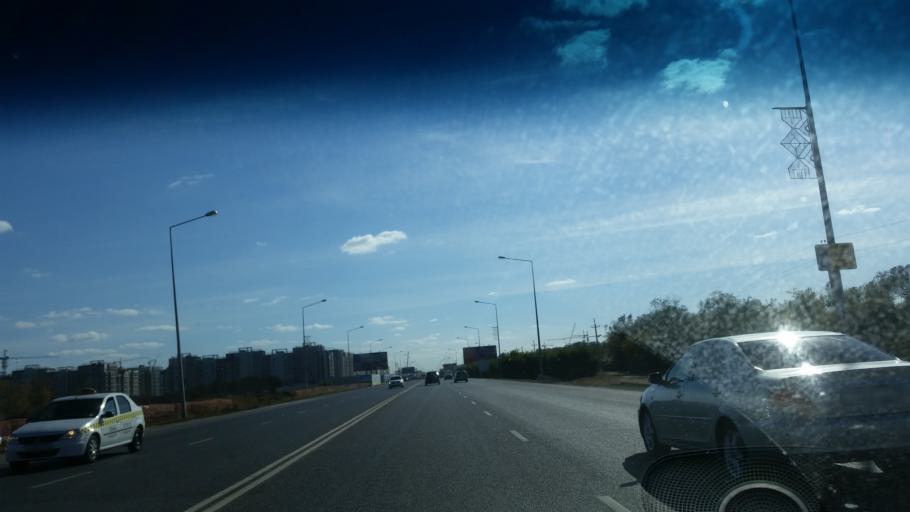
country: KZ
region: Astana Qalasy
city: Astana
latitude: 51.1029
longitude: 71.4074
